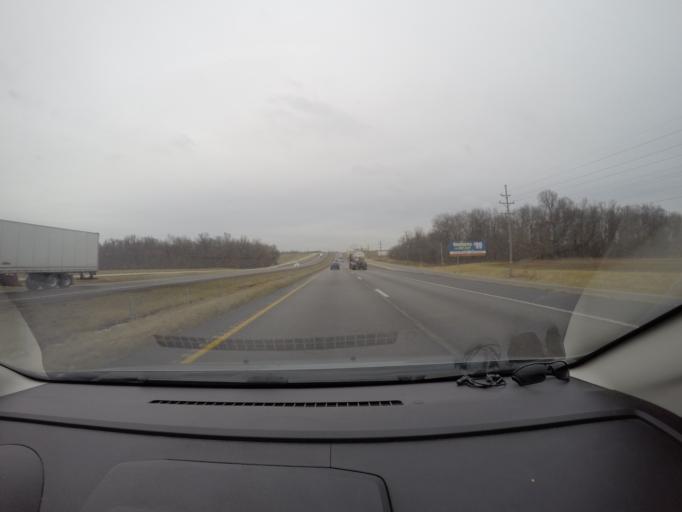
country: US
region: Missouri
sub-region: Warren County
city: Warrenton
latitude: 38.8459
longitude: -91.2614
